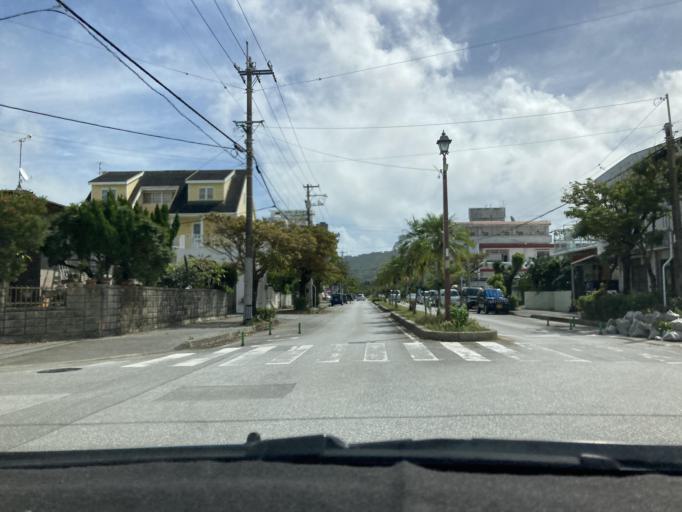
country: JP
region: Okinawa
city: Ginowan
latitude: 26.1766
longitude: 127.7757
